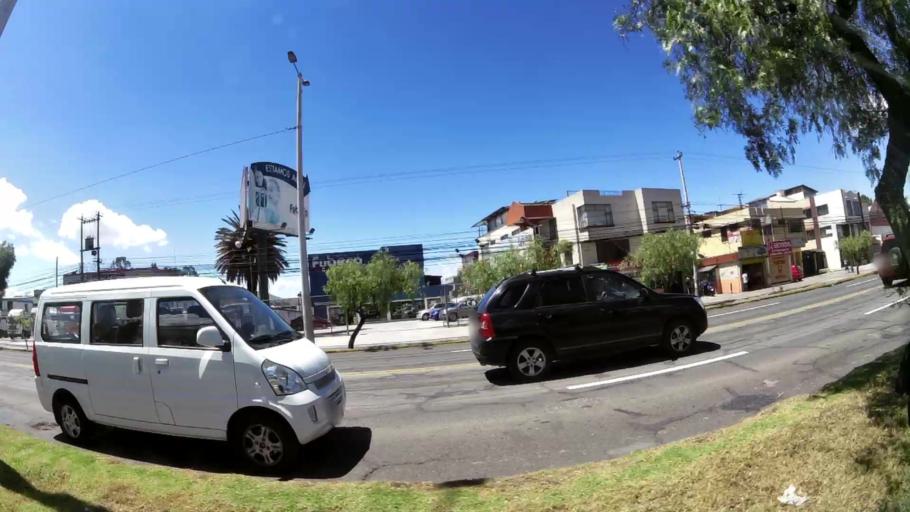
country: EC
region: Pichincha
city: Quito
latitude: -0.1522
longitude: -78.4845
